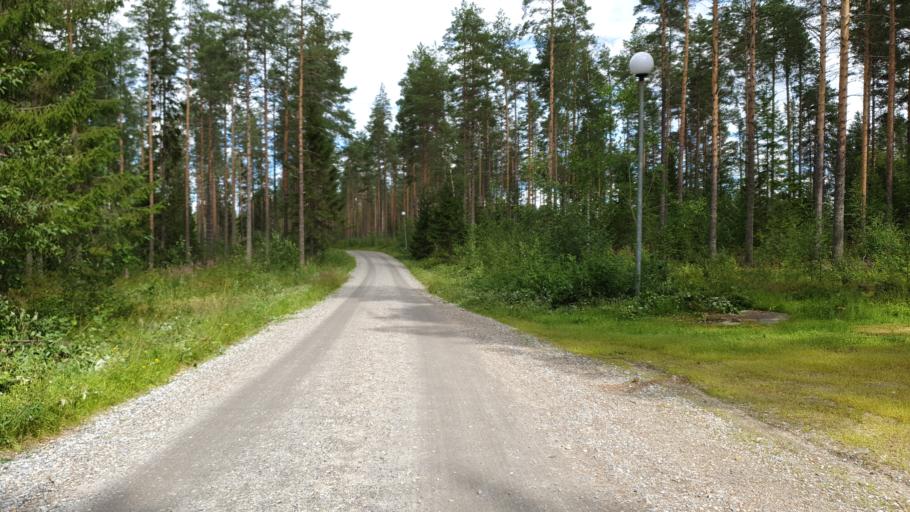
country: FI
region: Kainuu
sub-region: Kehys-Kainuu
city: Kuhmo
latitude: 64.3902
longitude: 29.8276
